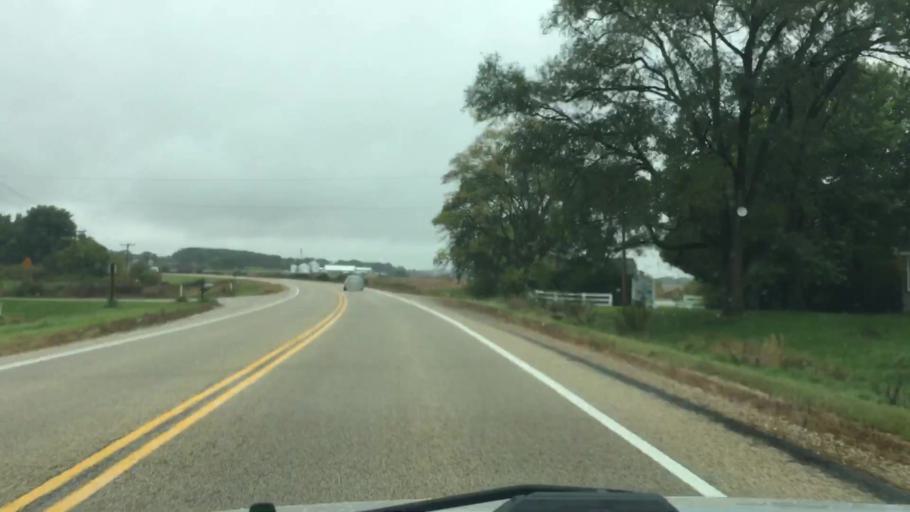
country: US
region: Wisconsin
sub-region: Jefferson County
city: Palmyra
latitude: 42.8601
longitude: -88.6572
